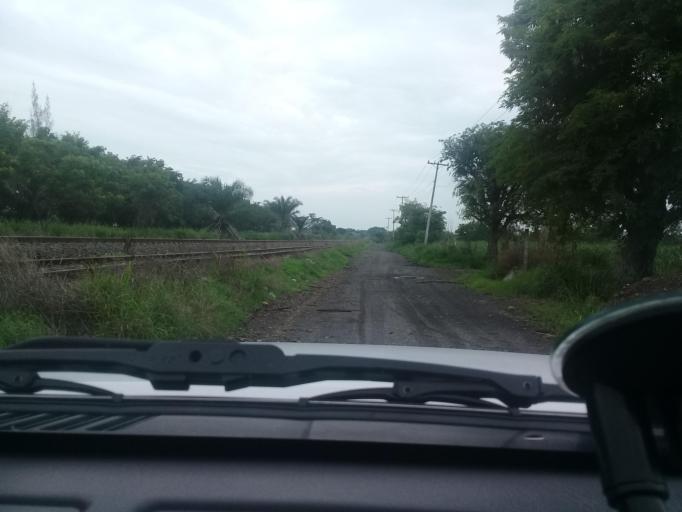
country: MX
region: Veracruz
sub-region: Puente Nacional
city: Cabezas
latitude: 19.3689
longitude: -96.3889
